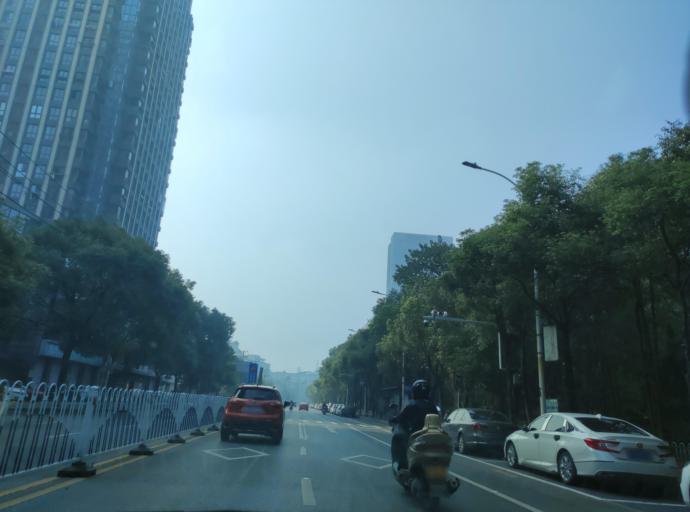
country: CN
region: Jiangxi Sheng
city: Pingxiang
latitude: 27.6462
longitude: 113.8506
